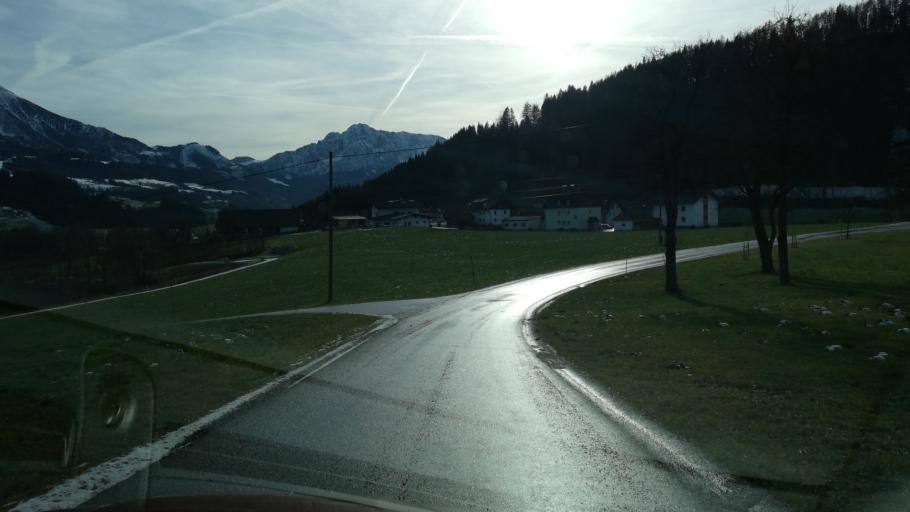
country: AT
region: Upper Austria
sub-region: Politischer Bezirk Kirchdorf an der Krems
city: Rossleithen
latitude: 47.7127
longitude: 14.3417
